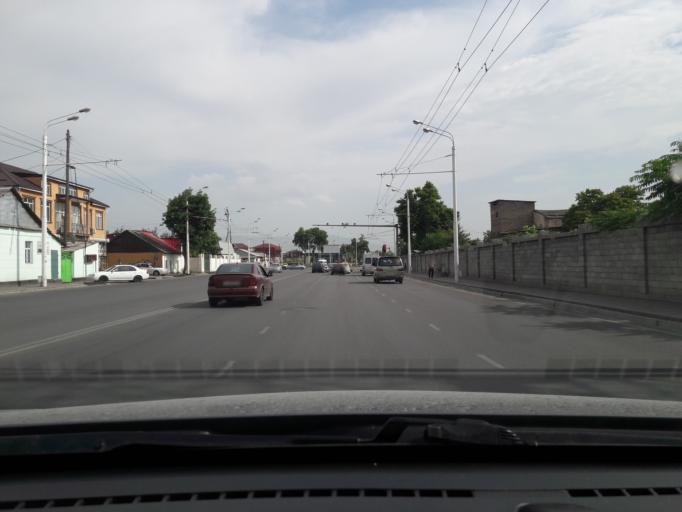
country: TJ
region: Dushanbe
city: Dushanbe
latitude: 38.5418
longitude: 68.7553
